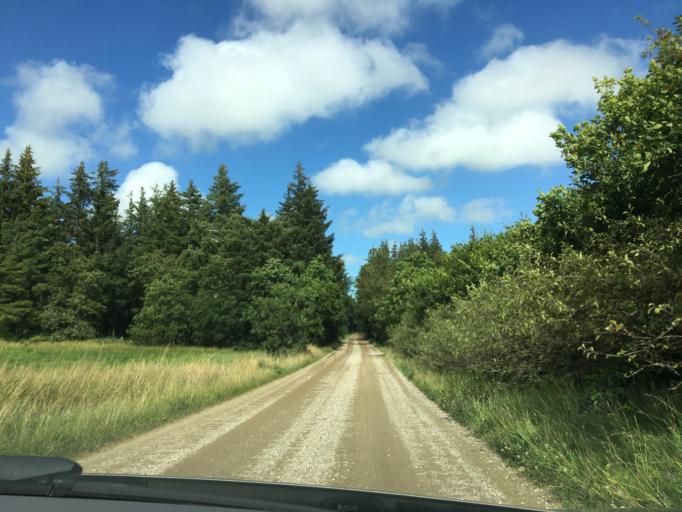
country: DK
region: South Denmark
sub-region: Varde Kommune
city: Oksbol
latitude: 55.7406
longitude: 8.2459
